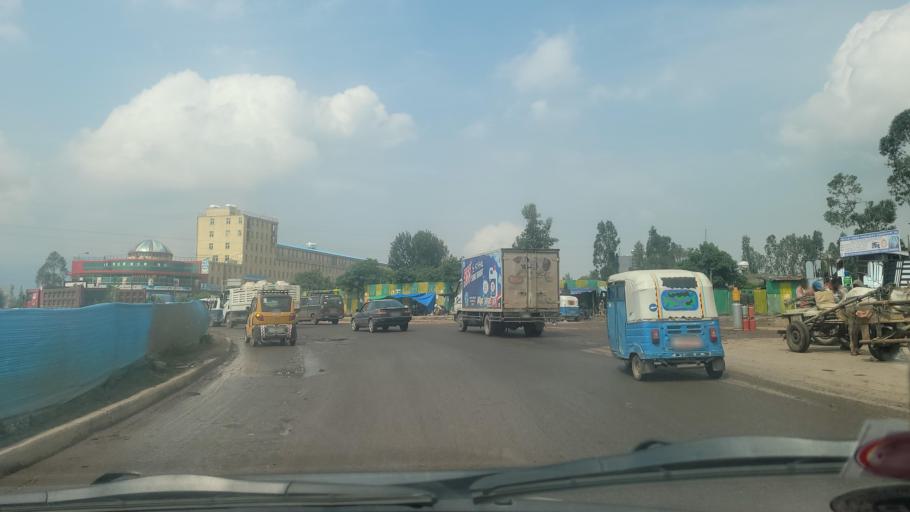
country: ET
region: Adis Abeba
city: Addis Ababa
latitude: 8.9548
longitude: 38.6964
